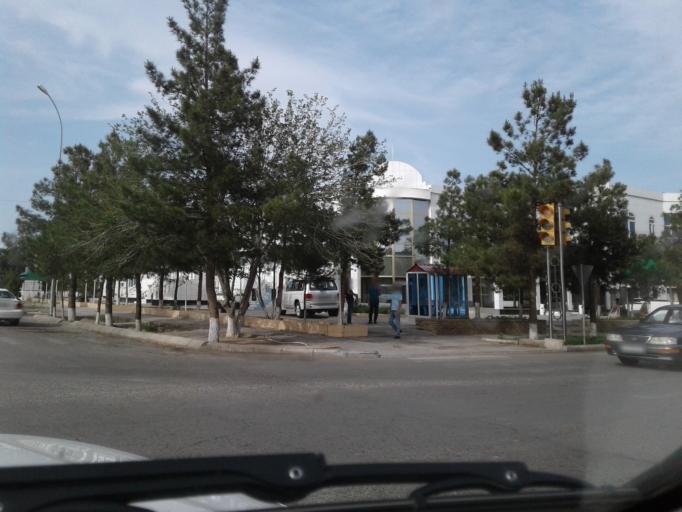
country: TM
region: Mary
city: Mary
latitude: 37.5919
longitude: 61.8341
